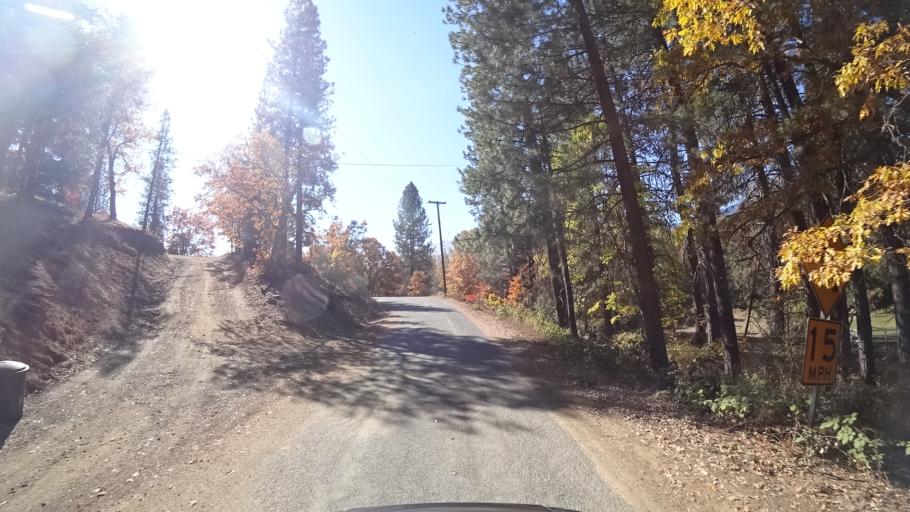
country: US
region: California
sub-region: Siskiyou County
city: Yreka
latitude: 41.6073
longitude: -122.9618
